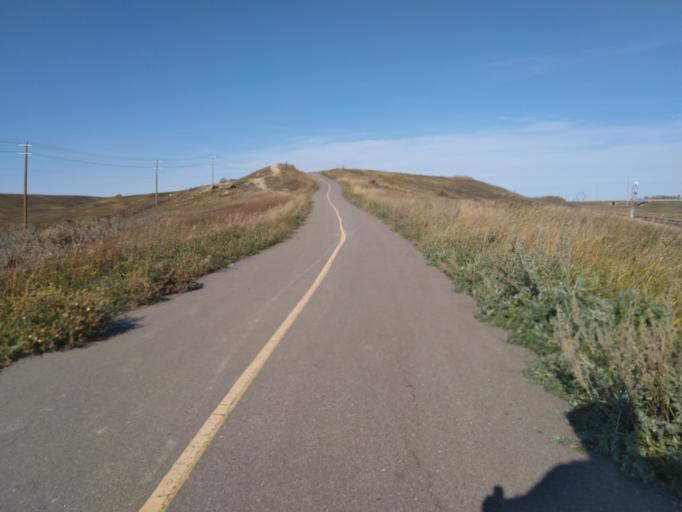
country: CA
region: Alberta
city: Calgary
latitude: 51.1326
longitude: -114.0473
